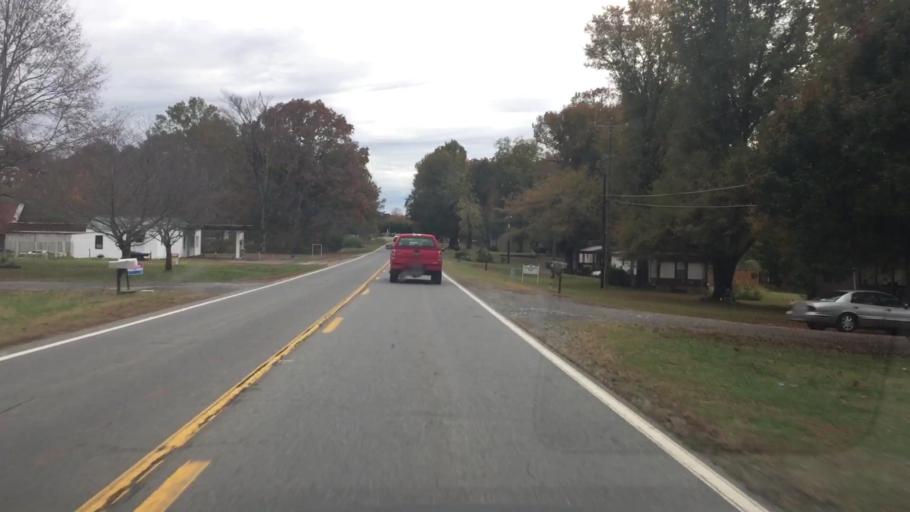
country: US
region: North Carolina
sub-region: Rockingham County
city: Reidsville
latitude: 36.3284
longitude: -79.7102
